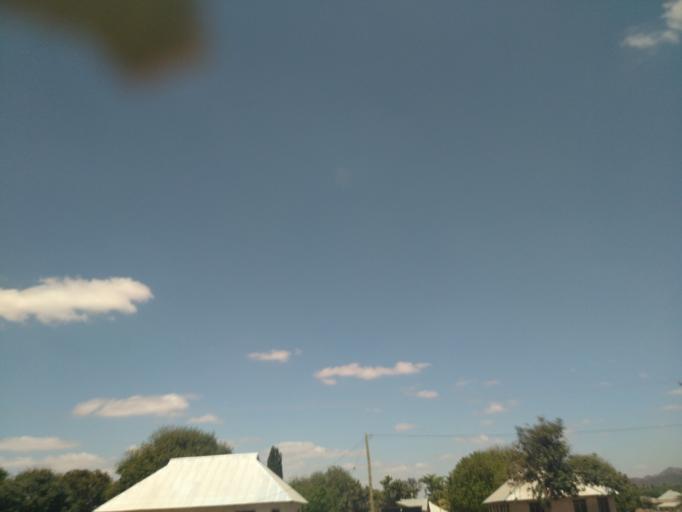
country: TZ
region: Dodoma
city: Dodoma
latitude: -6.1831
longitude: 35.7325
